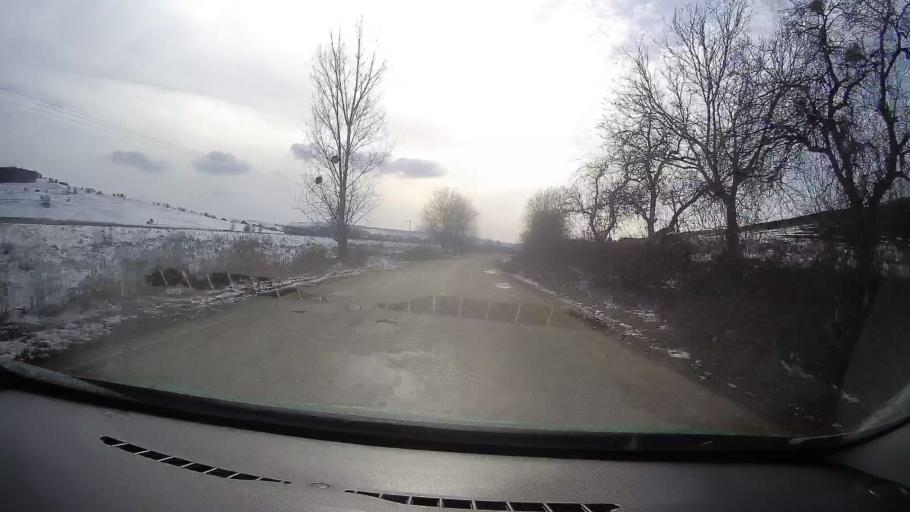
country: RO
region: Sibiu
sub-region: Comuna Bradeni
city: Bradeni
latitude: 46.0687
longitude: 24.8029
